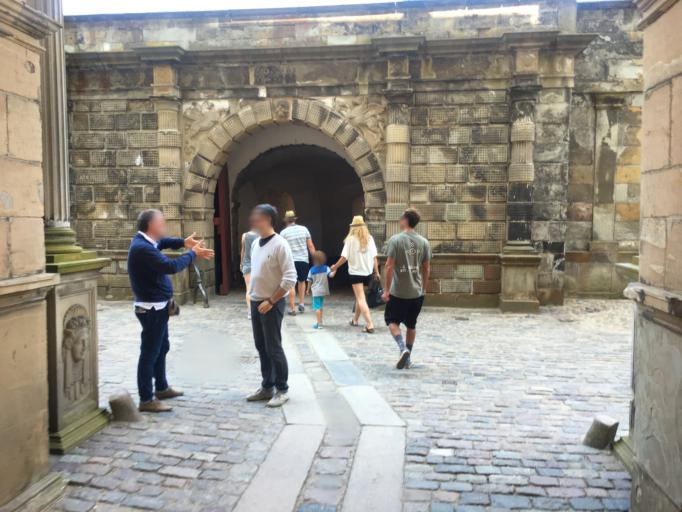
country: DK
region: Capital Region
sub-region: Helsingor Kommune
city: Helsingor
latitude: 56.0394
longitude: 12.6218
